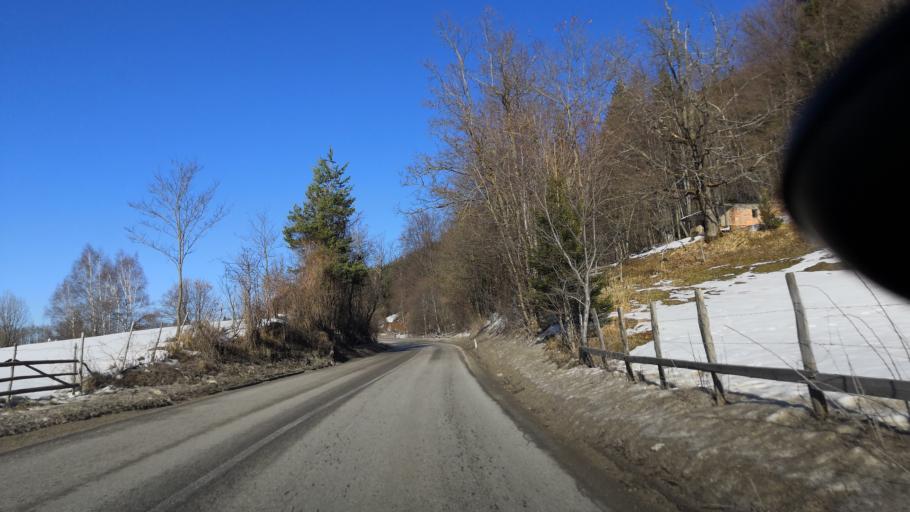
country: BA
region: Republika Srpska
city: Pale
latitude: 43.8996
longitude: 18.6358
